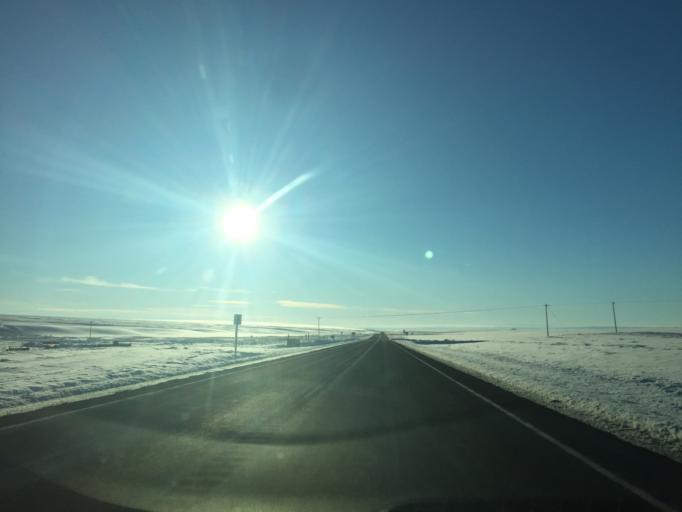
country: US
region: Washington
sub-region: Okanogan County
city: Coulee Dam
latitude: 47.6910
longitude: -118.9735
